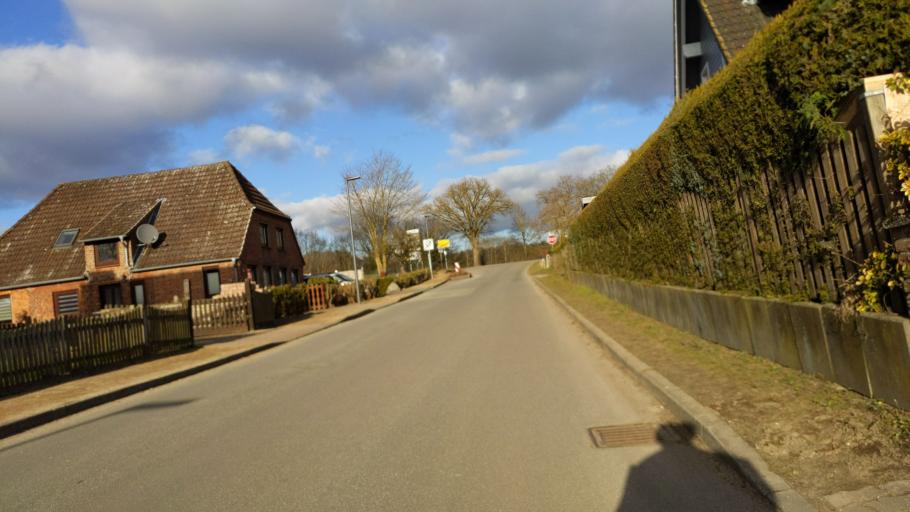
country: DE
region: Schleswig-Holstein
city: Susel
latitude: 54.0845
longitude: 10.7156
